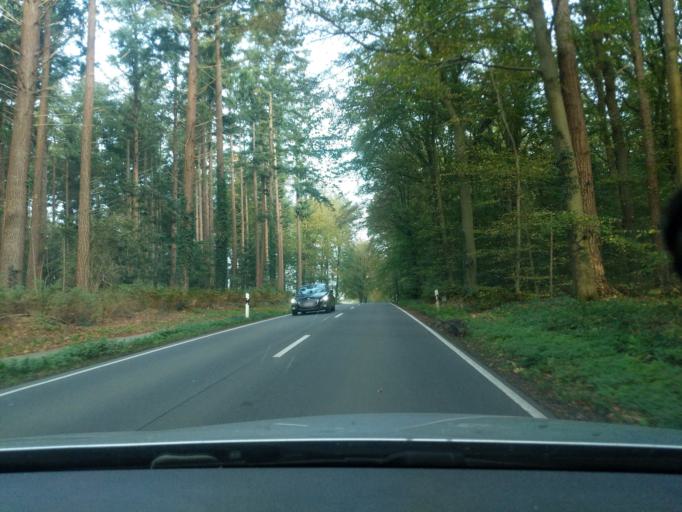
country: DE
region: Lower Saxony
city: Kranenburg
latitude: 53.6263
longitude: 9.1950
